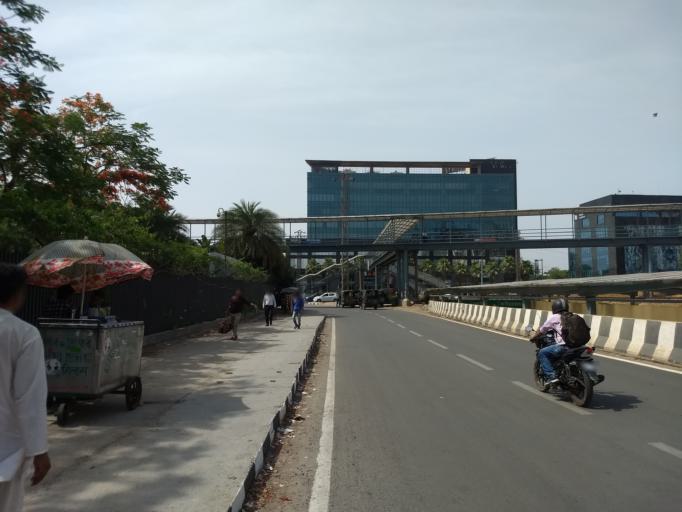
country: IN
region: Haryana
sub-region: Gurgaon
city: Gurgaon
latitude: 28.4772
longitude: 77.0714
